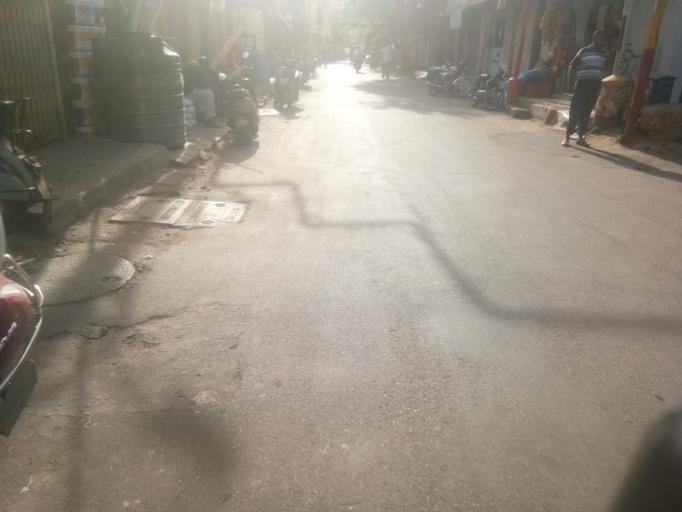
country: IN
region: Karnataka
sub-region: Bangalore Urban
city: Bangalore
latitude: 13.0035
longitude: 77.6026
